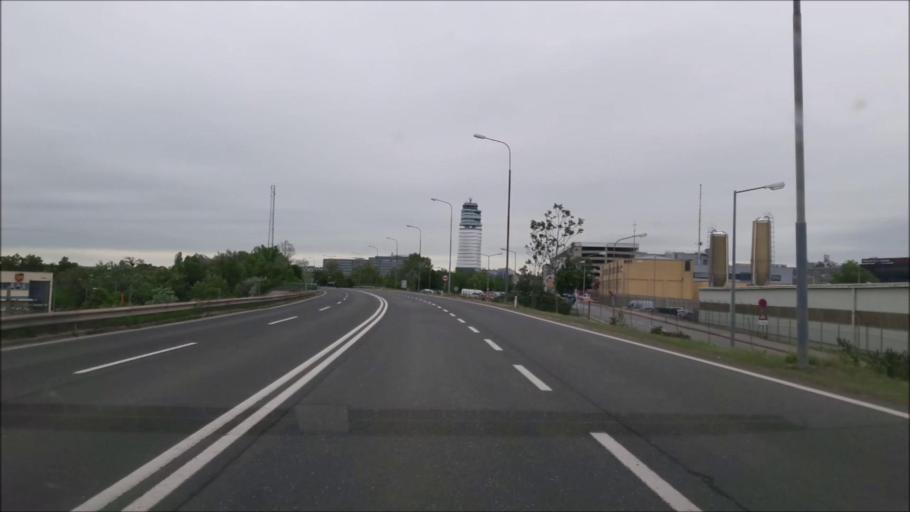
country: AT
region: Lower Austria
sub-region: Politischer Bezirk Wien-Umgebung
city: Rauchenwarth
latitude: 48.1261
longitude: 16.5514
